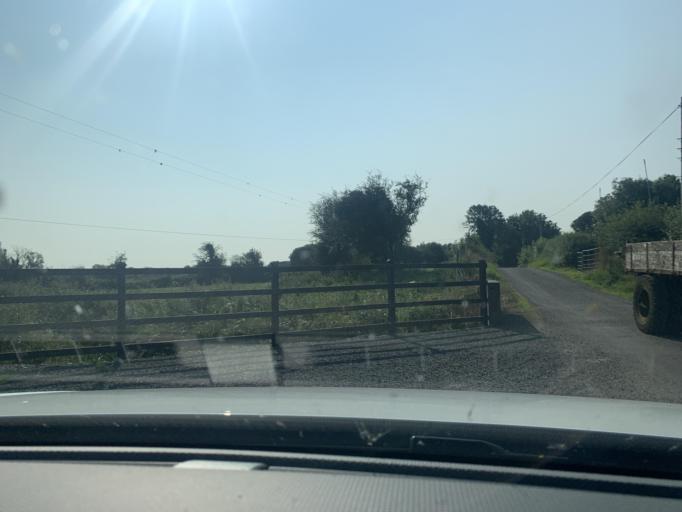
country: IE
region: Connaught
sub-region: Maigh Eo
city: Ballyhaunis
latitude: 53.8005
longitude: -8.7442
